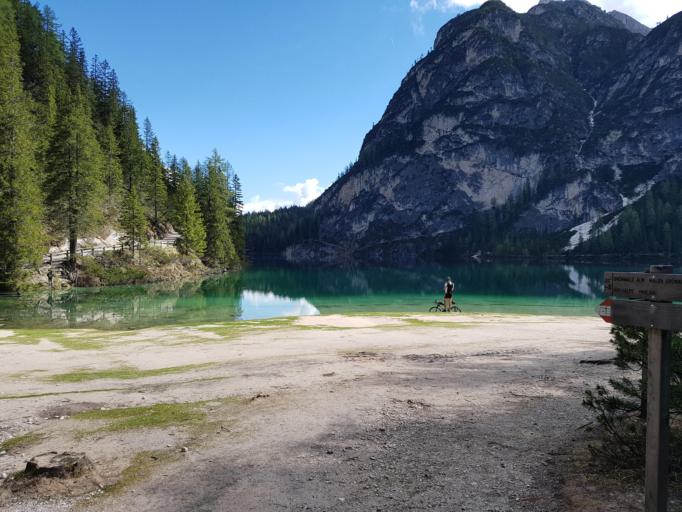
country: IT
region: Trentino-Alto Adige
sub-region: Bolzano
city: Braies
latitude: 46.6908
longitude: 12.0806
